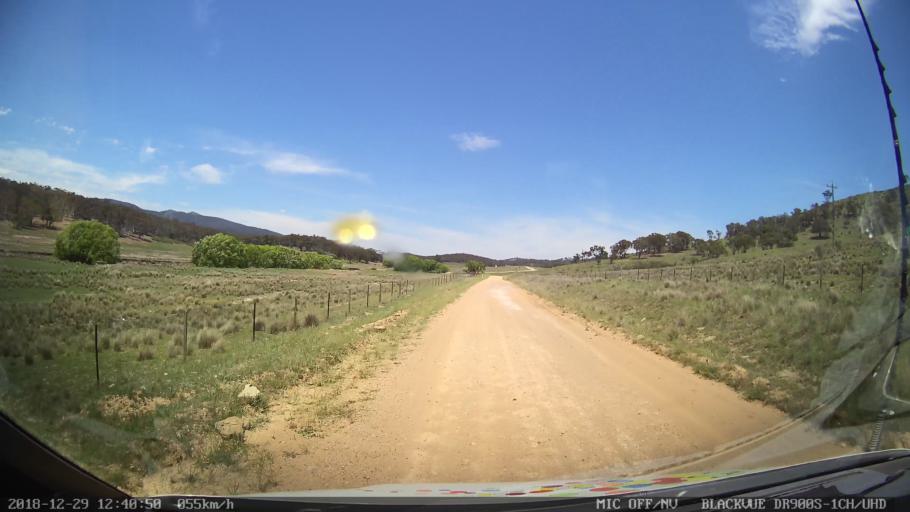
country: AU
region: Australian Capital Territory
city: Macarthur
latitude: -35.6043
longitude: 149.2236
